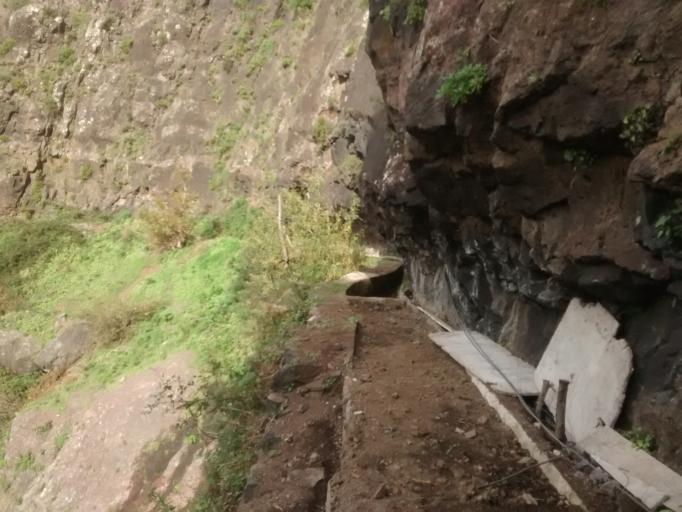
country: PT
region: Madeira
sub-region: Camara de Lobos
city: Curral das Freiras
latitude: 32.7208
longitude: -17.0243
